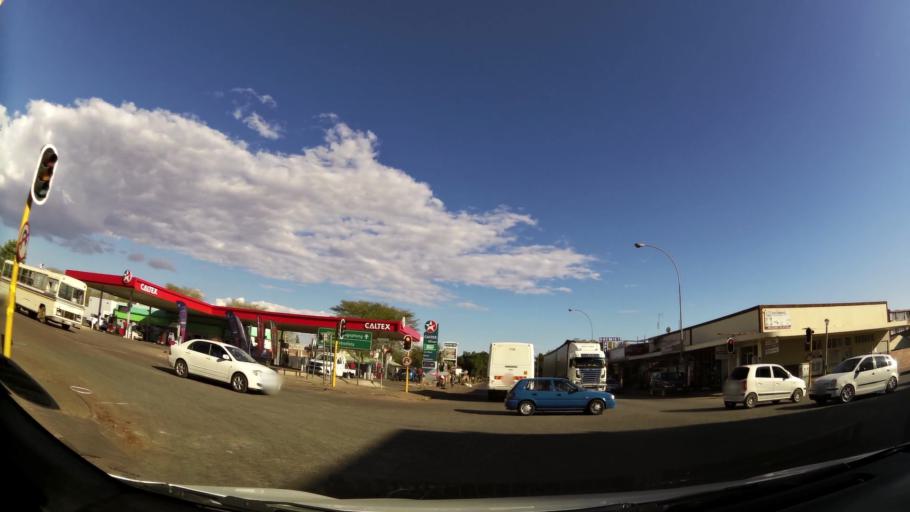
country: ZA
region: Limpopo
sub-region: Waterberg District Municipality
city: Mokopane
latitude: -24.1861
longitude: 29.0121
